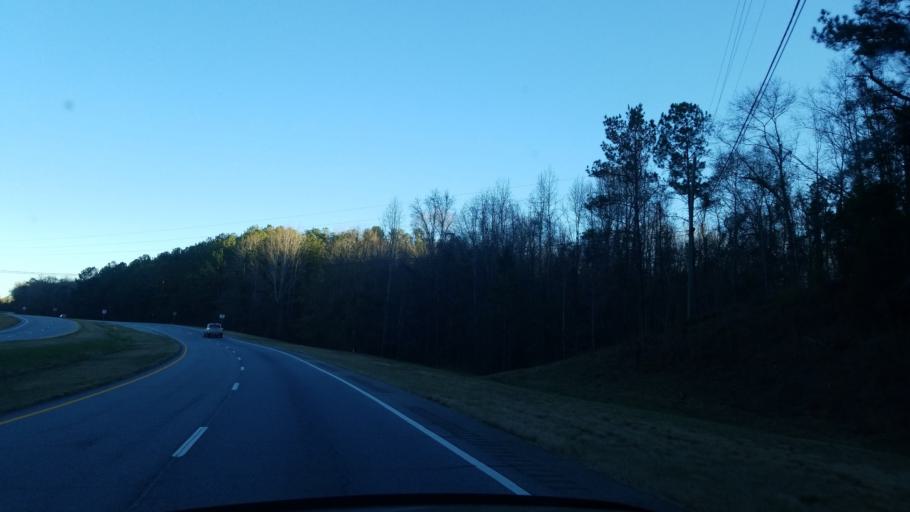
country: US
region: Georgia
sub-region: Chattahoochee County
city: Cusseta
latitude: 32.2648
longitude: -84.7406
